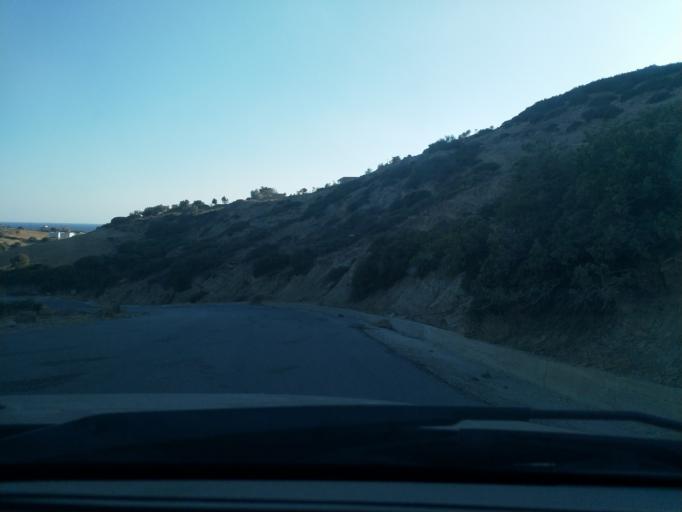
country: GR
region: Crete
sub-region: Nomos Rethymnis
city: Agia Galini
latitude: 35.1201
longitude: 24.5584
